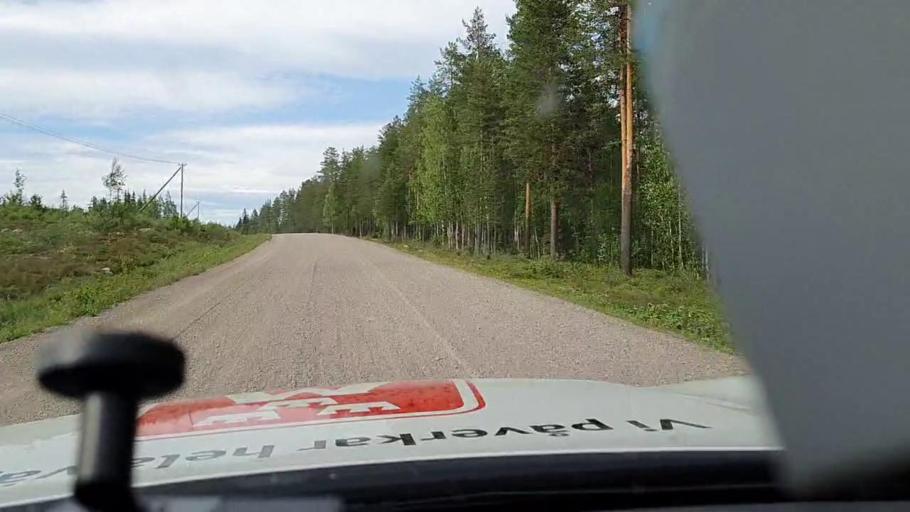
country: SE
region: Norrbotten
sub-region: Alvsbyns Kommun
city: AElvsbyn
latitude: 66.1303
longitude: 20.9987
